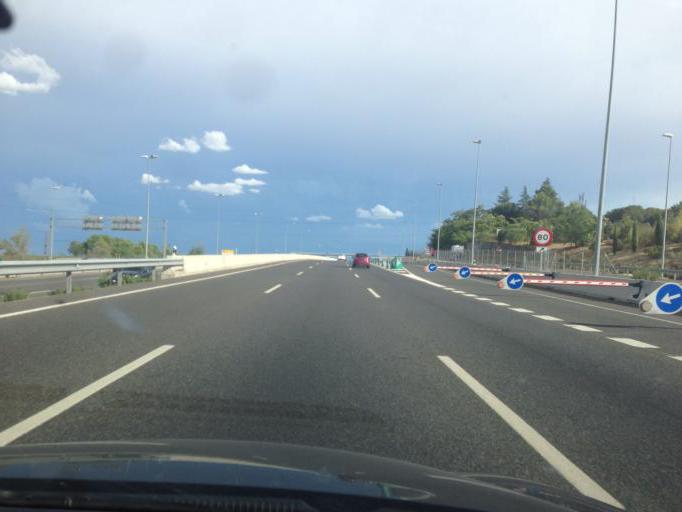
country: ES
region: Madrid
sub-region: Provincia de Madrid
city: Las Rozas de Madrid
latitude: 40.5069
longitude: -3.8772
